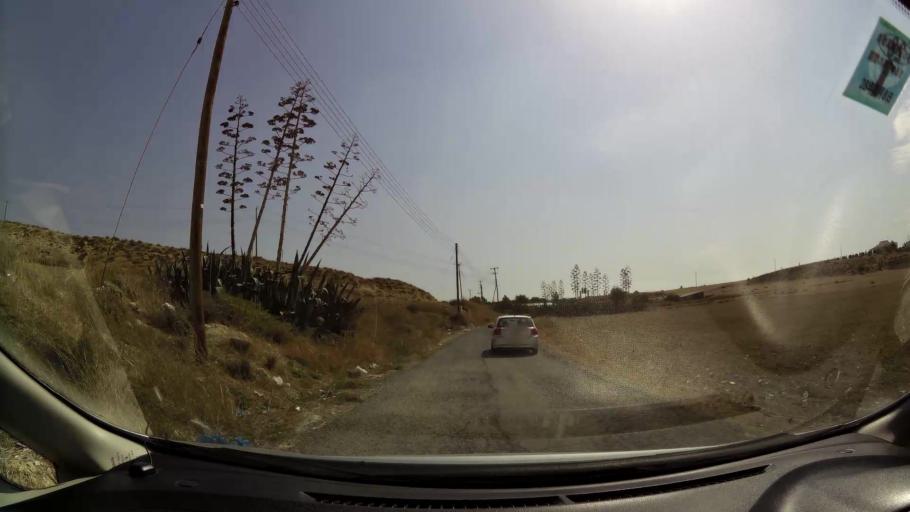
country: CY
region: Larnaka
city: Aradippou
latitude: 34.9583
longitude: 33.5750
